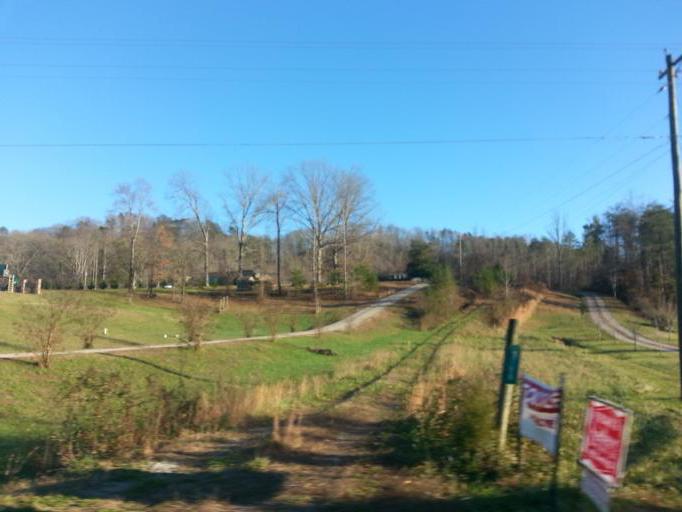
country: US
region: Tennessee
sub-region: Anderson County
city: Clinton
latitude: 36.1451
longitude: -84.1812
